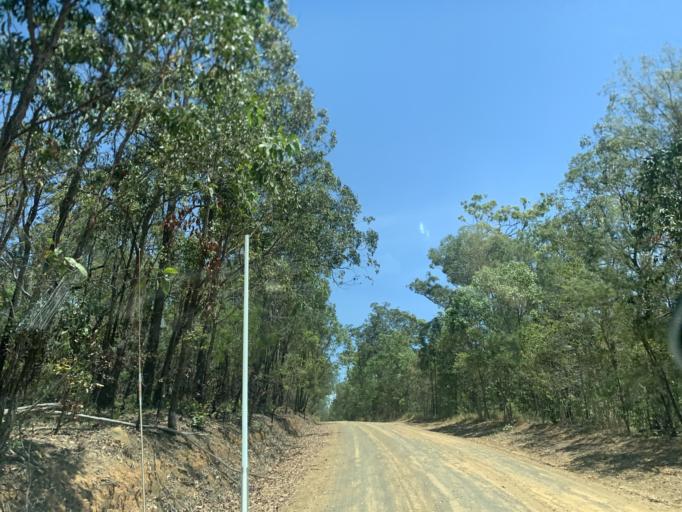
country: AU
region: Queensland
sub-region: Tablelands
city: Kuranda
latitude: -16.9194
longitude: 145.5913
